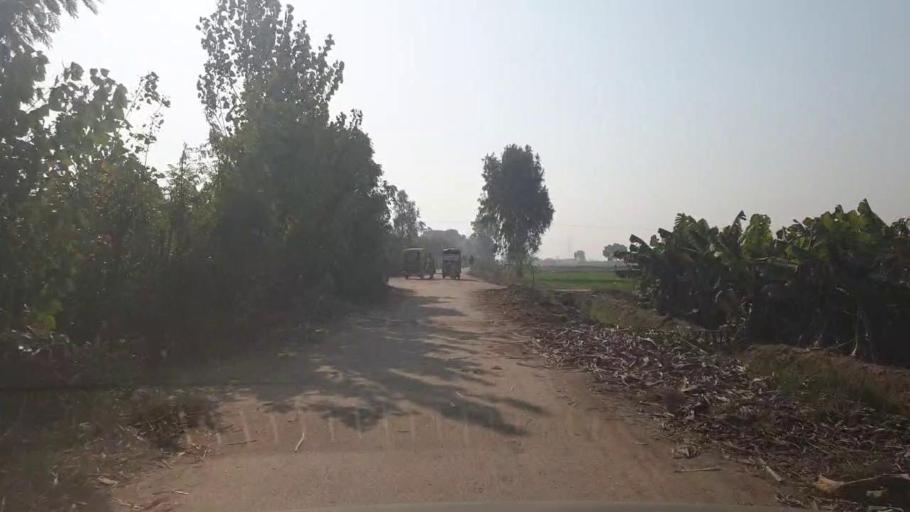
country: PK
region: Sindh
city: Tando Allahyar
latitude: 25.4650
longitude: 68.7630
